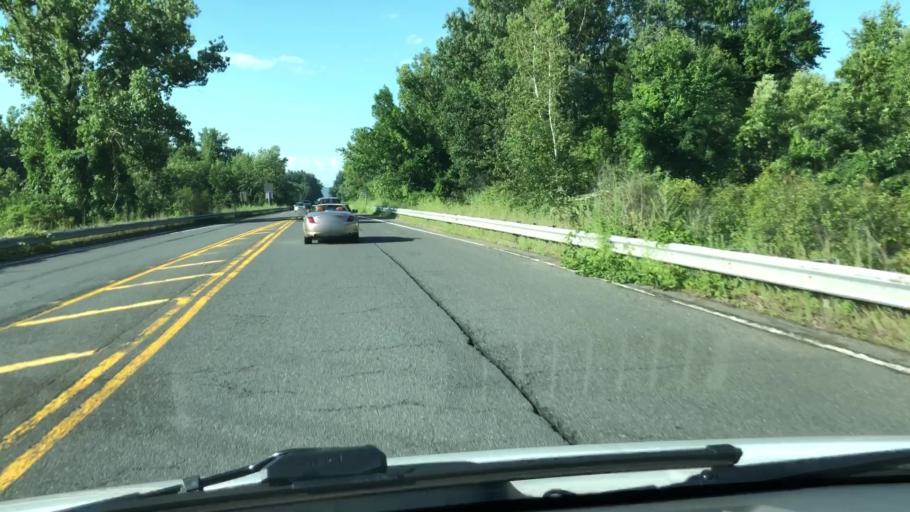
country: US
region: Massachusetts
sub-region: Hampshire County
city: North Amherst
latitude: 42.4078
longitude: -72.5381
